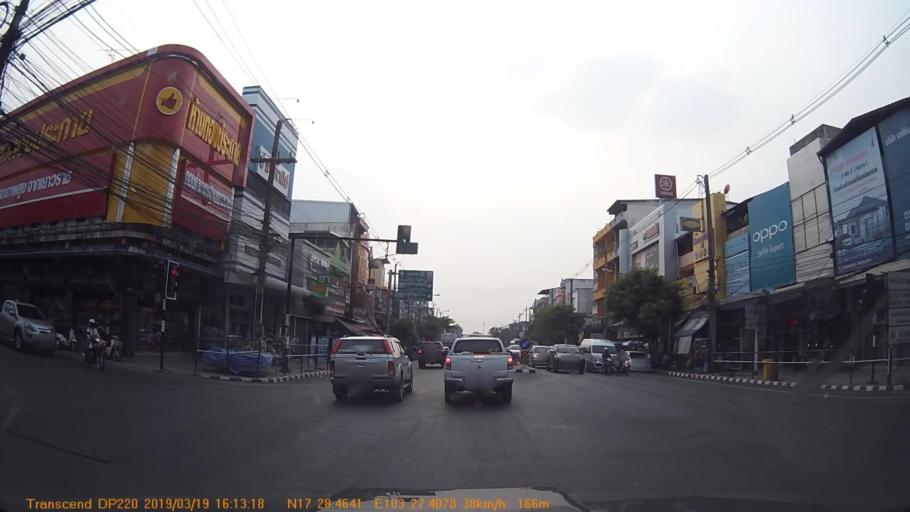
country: TH
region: Sakon Nakhon
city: Sawang Daen Din
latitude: 17.4744
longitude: 103.4565
